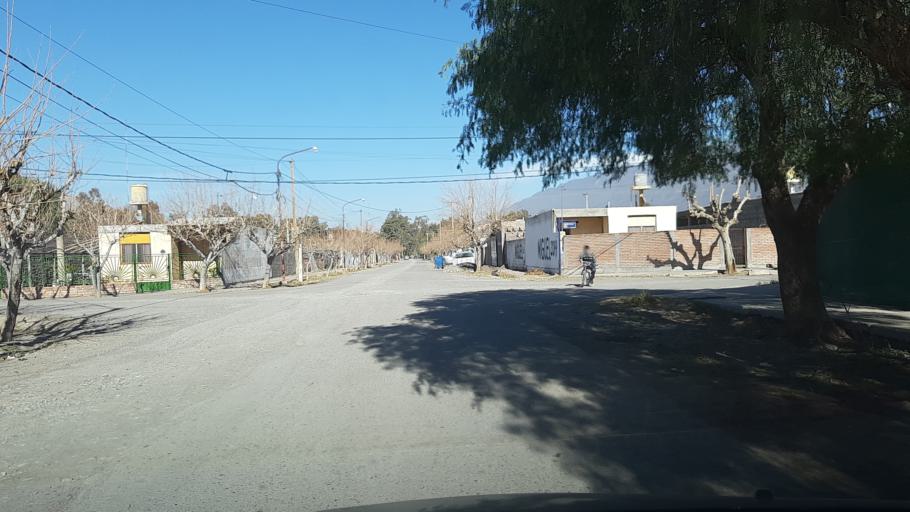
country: AR
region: San Juan
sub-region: Departamento de Zonda
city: Zonda
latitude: -31.5478
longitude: -68.7275
